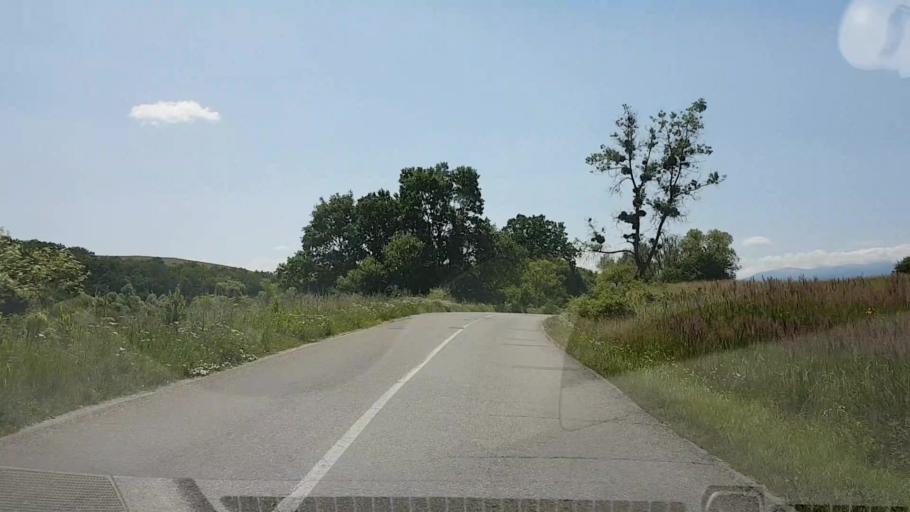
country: RO
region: Brasov
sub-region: Comuna Voila
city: Voila
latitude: 45.8667
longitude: 24.8245
